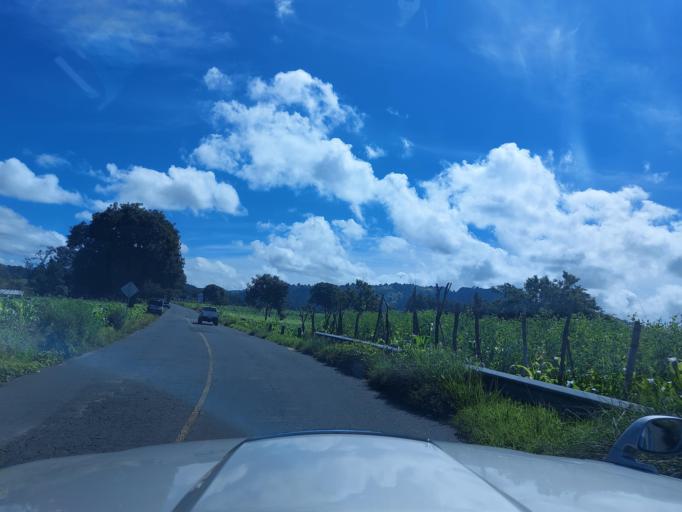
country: GT
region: Chimaltenango
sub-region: Municipio de Santa Cruz Balanya
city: Santa Cruz Balanya
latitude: 14.6998
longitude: -90.8993
